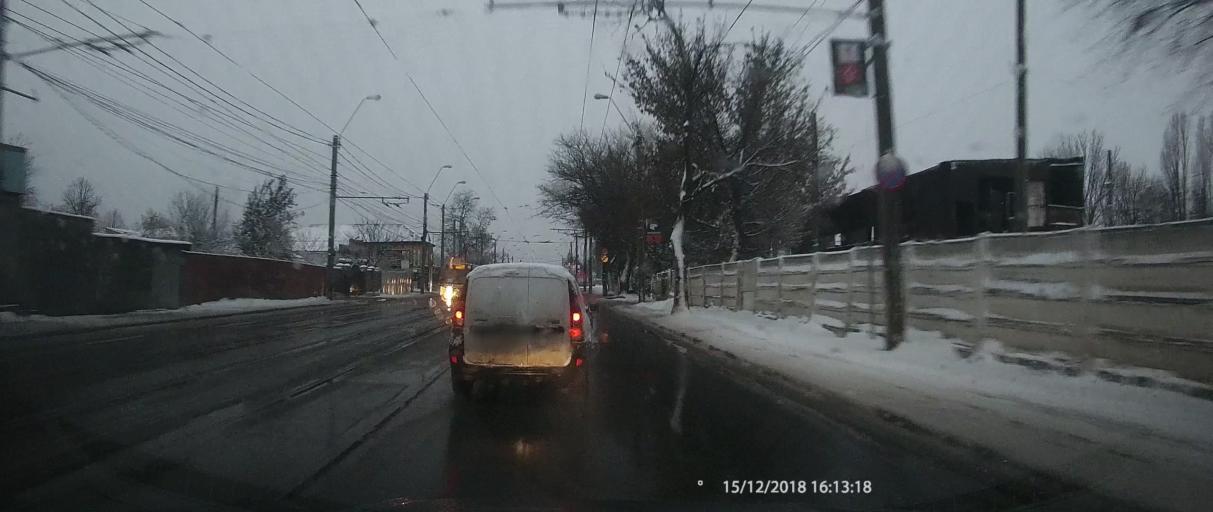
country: RO
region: Galati
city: Galati
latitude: 45.4644
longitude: 28.0333
